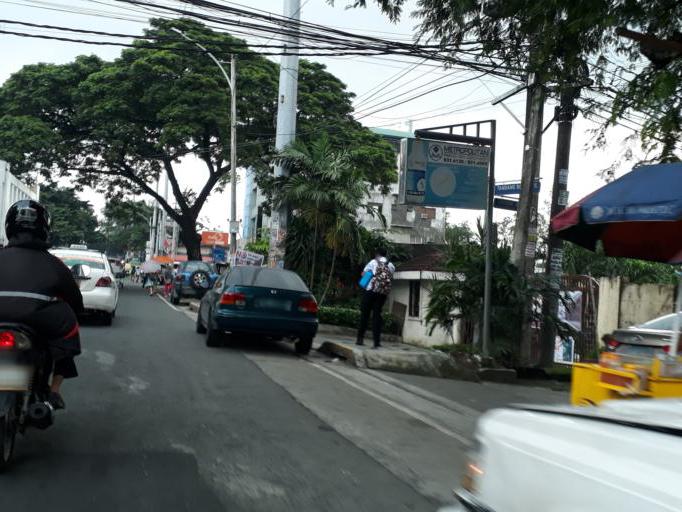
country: PH
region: Metro Manila
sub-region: Quezon City
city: Quezon City
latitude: 14.6691
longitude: 121.0542
